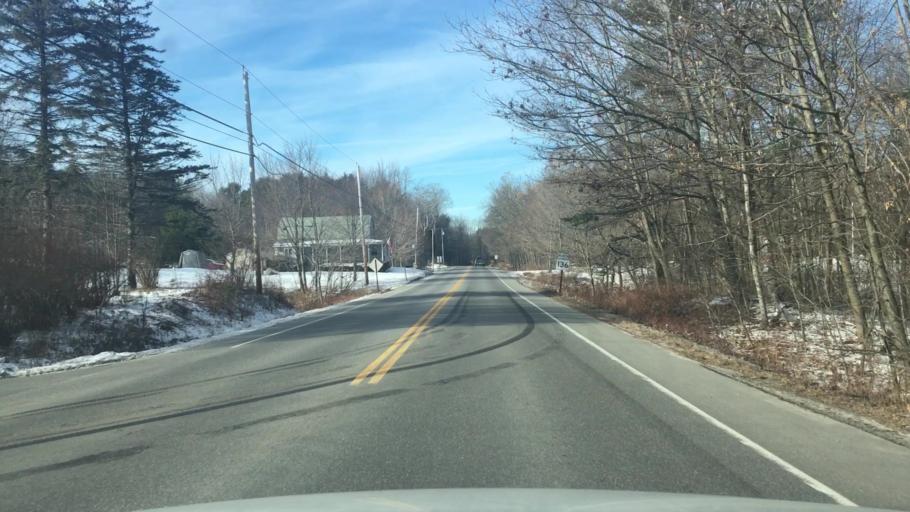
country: US
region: Maine
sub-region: Androscoggin County
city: Lisbon
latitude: 43.9838
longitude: -70.1328
